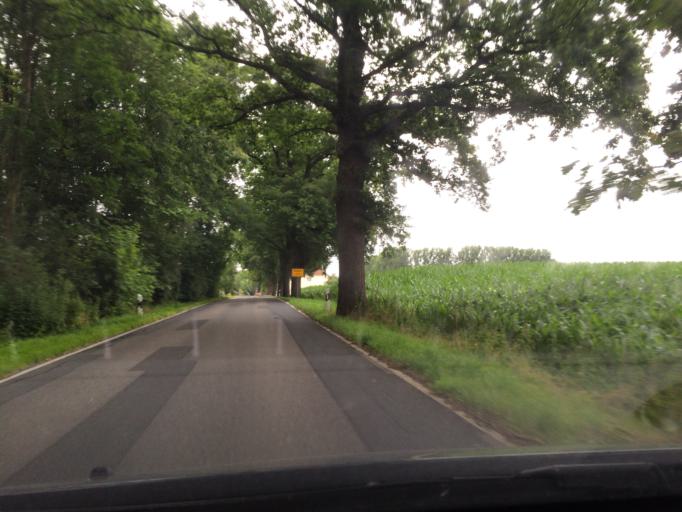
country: DE
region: Mecklenburg-Vorpommern
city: Prohn
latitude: 54.3984
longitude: 13.0096
